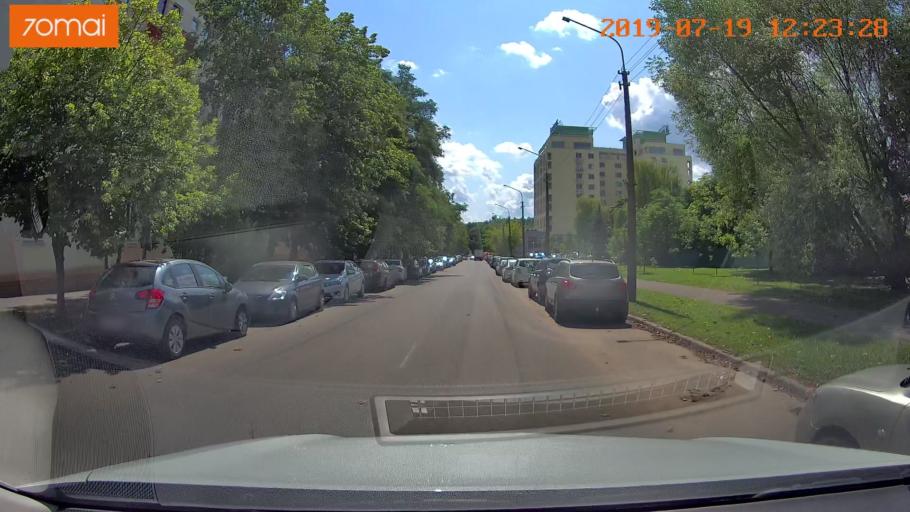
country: BY
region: Minsk
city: Minsk
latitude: 53.9278
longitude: 27.6182
